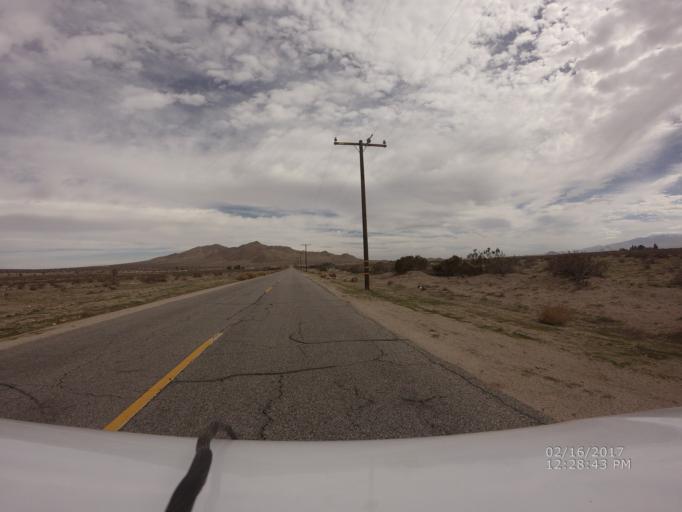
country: US
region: California
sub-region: Los Angeles County
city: Lake Los Angeles
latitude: 34.6679
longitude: -117.8372
